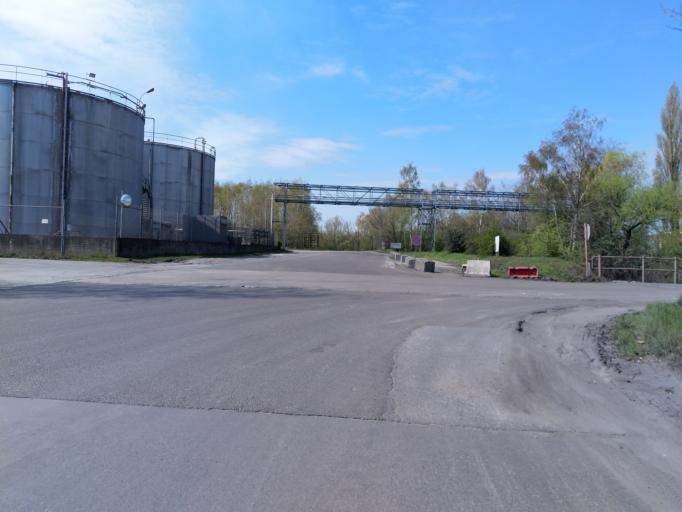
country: BE
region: Wallonia
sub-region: Province du Hainaut
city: Mons
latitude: 50.4716
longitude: 3.9896
